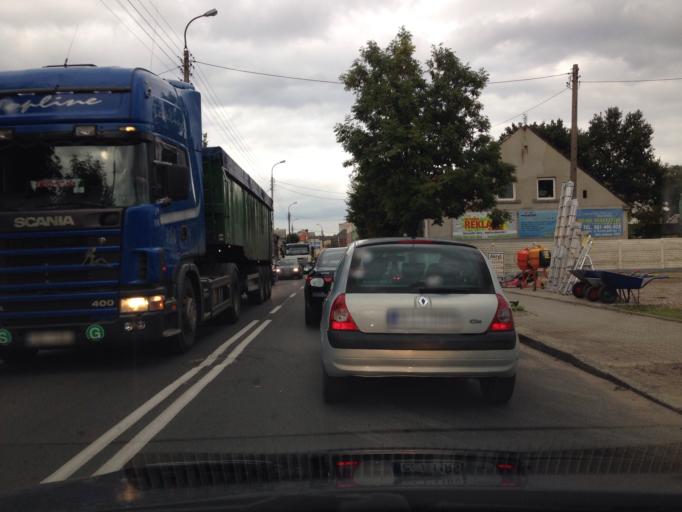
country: PL
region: Kujawsko-Pomorskie
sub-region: Powiat lipnowski
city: Lipno
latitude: 52.8407
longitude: 19.1759
